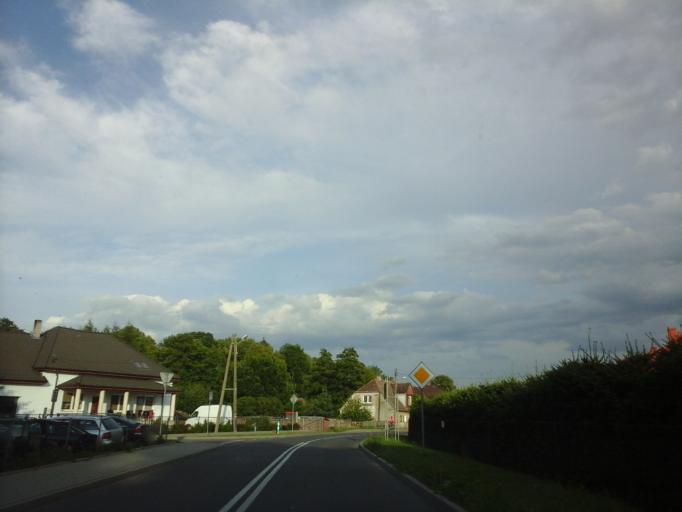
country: PL
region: West Pomeranian Voivodeship
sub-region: Powiat kamienski
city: Golczewo
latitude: 53.8629
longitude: 14.9093
